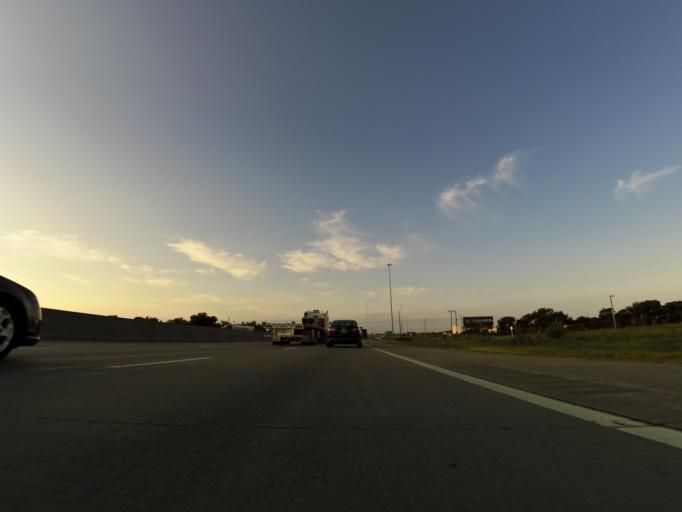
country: US
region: Kansas
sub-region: Sedgwick County
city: Wichita
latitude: 37.7315
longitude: -97.3168
